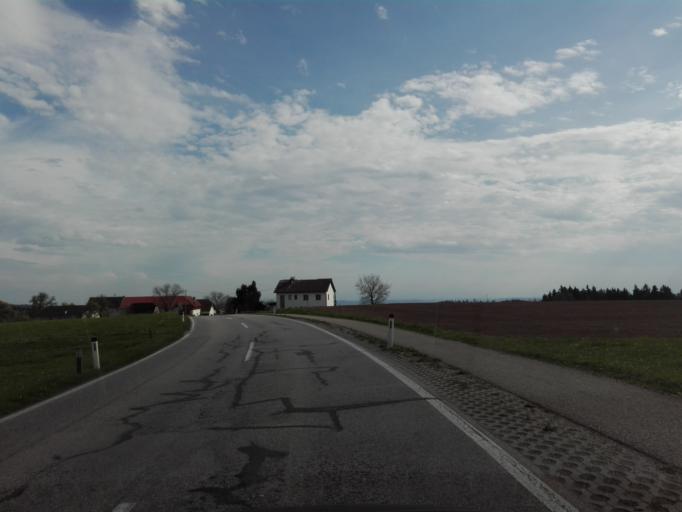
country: AT
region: Upper Austria
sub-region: Politischer Bezirk Rohrbach
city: Kleinzell im Muehlkreis
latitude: 48.4327
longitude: 14.0320
